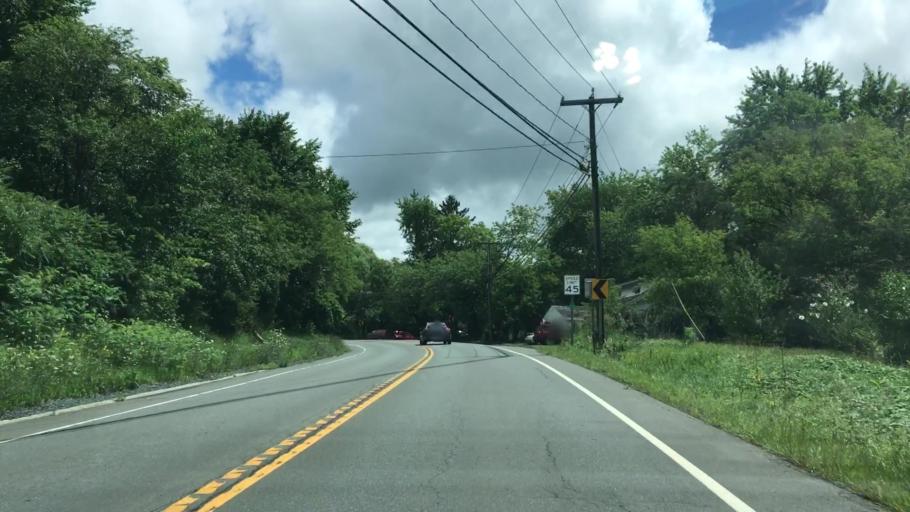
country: US
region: New York
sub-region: Rensselaer County
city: Hoosick Falls
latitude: 42.8445
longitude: -73.4567
